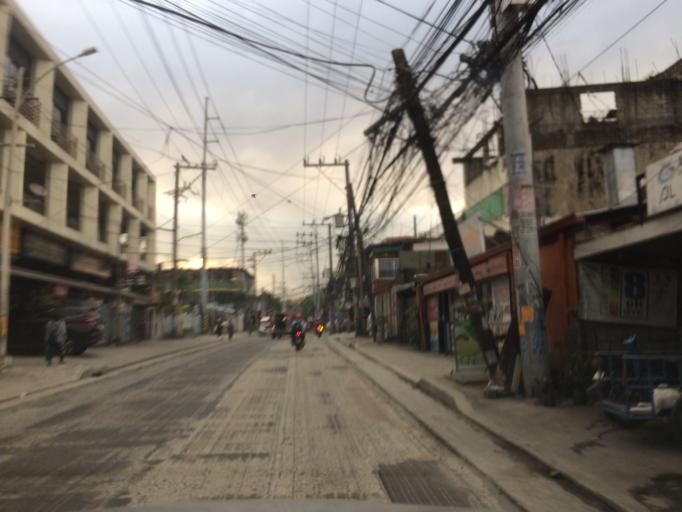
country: PH
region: Calabarzon
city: Bagong Pagasa
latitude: 14.6767
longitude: 121.0344
